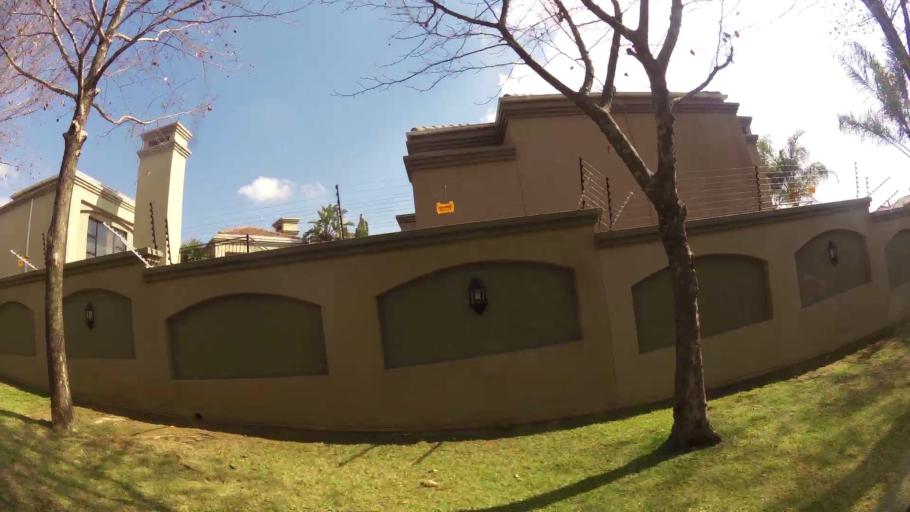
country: ZA
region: Gauteng
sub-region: City of Johannesburg Metropolitan Municipality
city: Midrand
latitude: -26.0241
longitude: 28.0729
